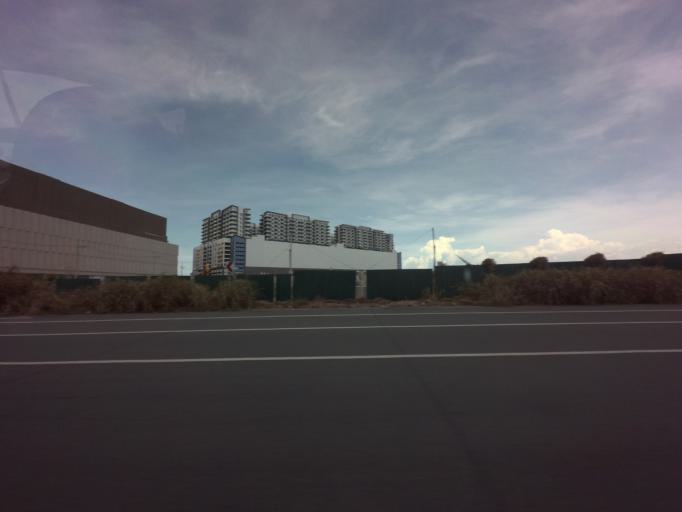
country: PH
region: Metro Manila
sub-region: Makati City
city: Makati City
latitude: 14.5222
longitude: 120.9858
